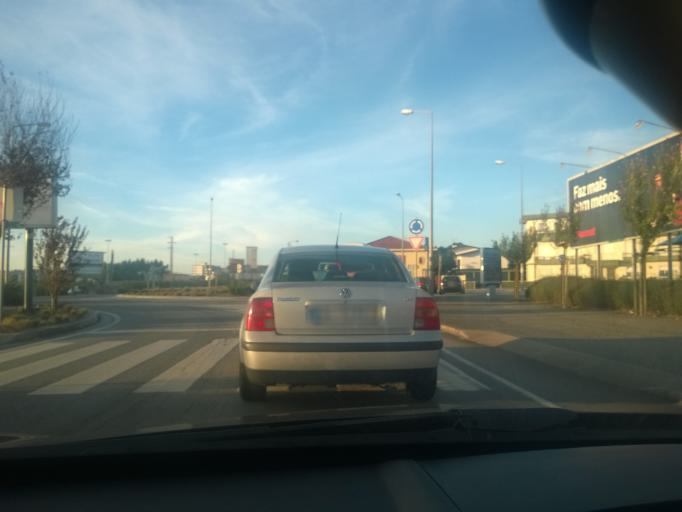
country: PT
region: Porto
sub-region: Maia
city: Anta
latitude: 41.2543
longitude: -8.6166
